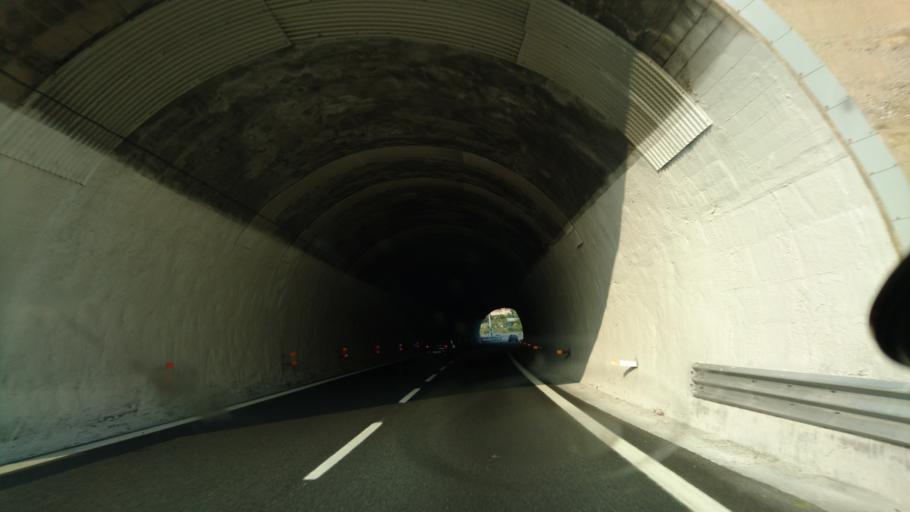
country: IT
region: Liguria
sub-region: Provincia di Savona
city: Valleggia
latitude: 44.3007
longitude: 8.4471
